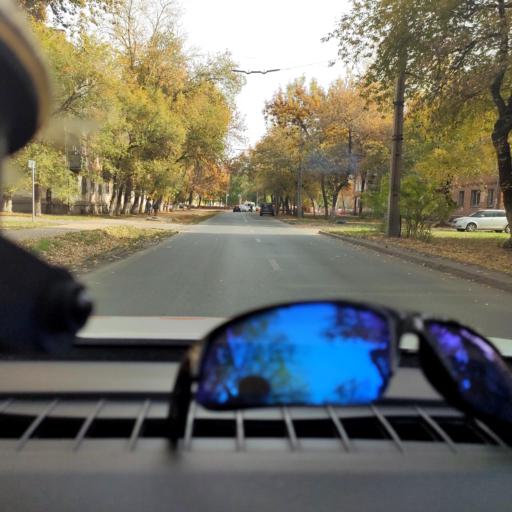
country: RU
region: Samara
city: Samara
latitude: 53.1175
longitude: 50.0827
